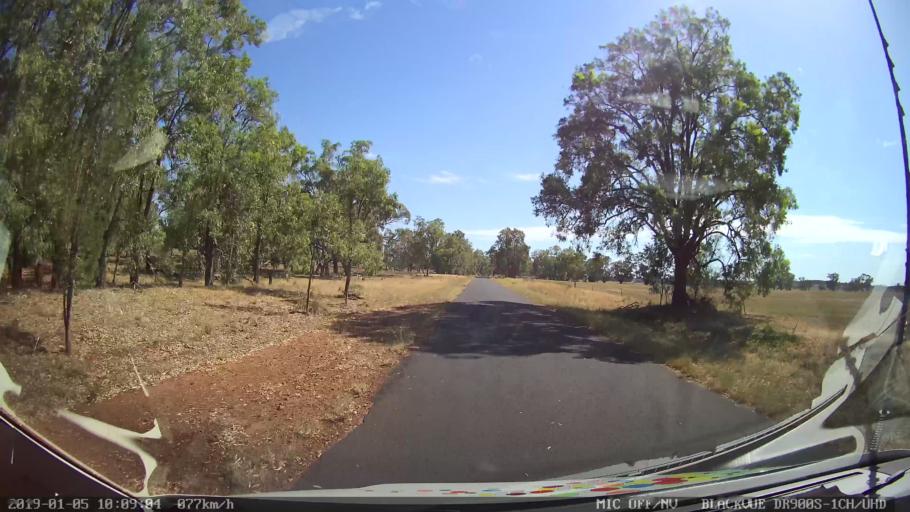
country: AU
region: New South Wales
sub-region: Gilgandra
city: Gilgandra
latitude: -31.6349
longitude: 148.8841
